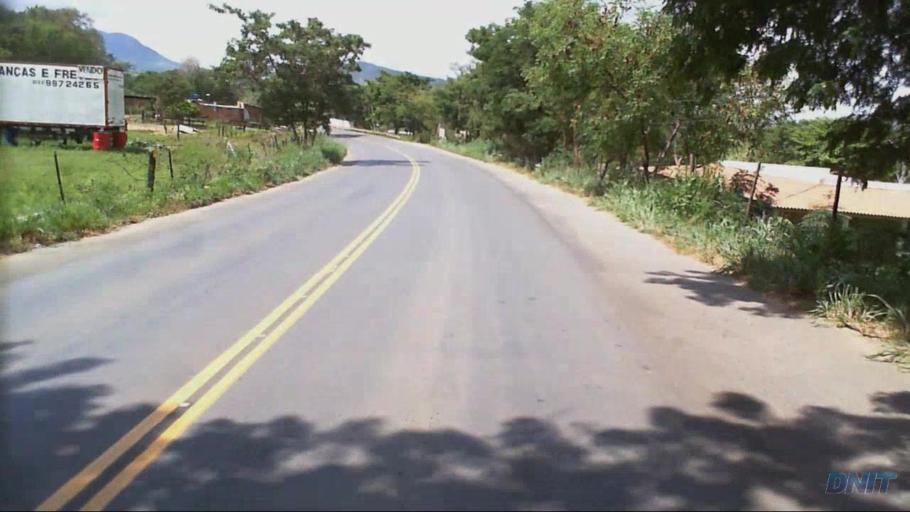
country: BR
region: Minas Gerais
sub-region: Governador Valadares
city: Governador Valadares
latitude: -18.9144
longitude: -42.0018
